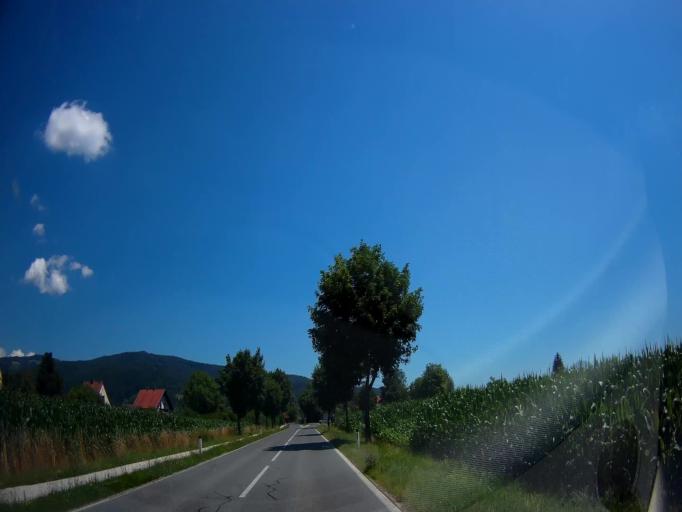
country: AT
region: Carinthia
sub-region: Politischer Bezirk Volkermarkt
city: Bleiburg/Pliberk
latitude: 46.5774
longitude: 14.7870
